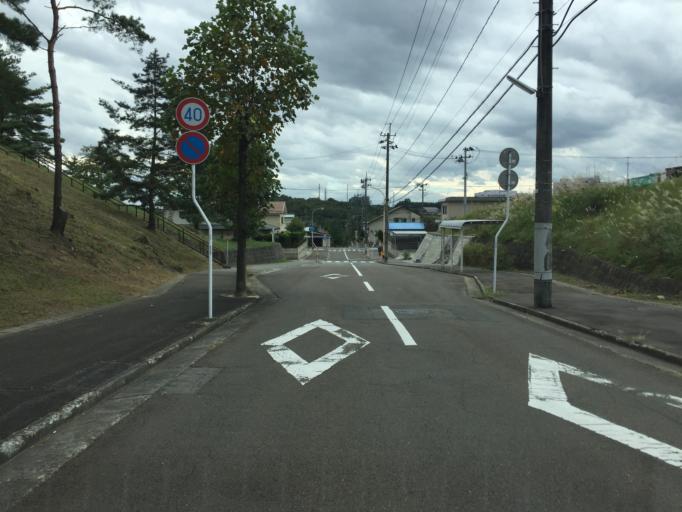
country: JP
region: Fukushima
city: Fukushima-shi
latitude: 37.6954
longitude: 140.4780
